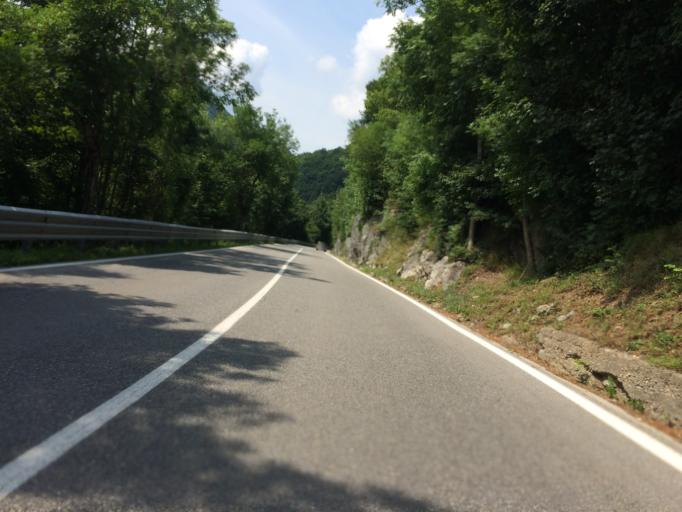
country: IT
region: Piedmont
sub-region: Provincia di Cuneo
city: Vernante
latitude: 44.2573
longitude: 7.5252
